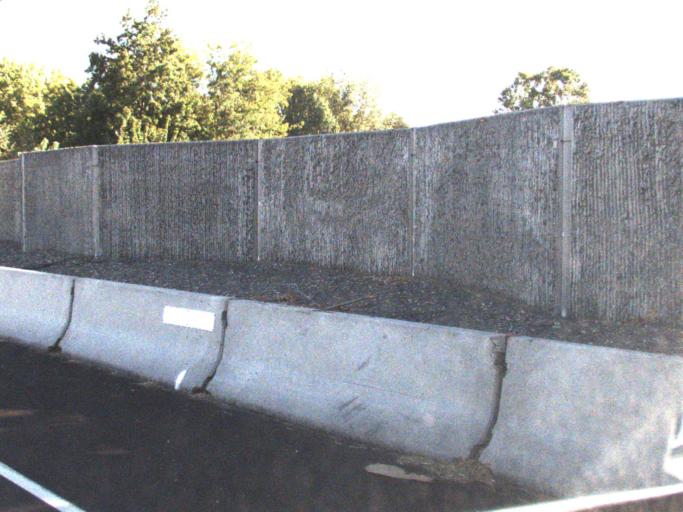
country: US
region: Washington
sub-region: Benton County
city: Richland
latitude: 46.3003
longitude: -119.2970
